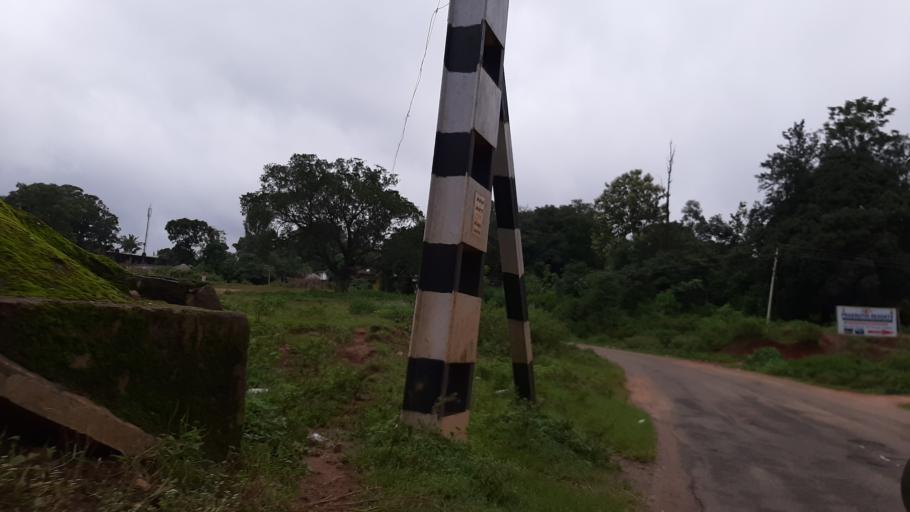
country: IN
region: Andhra Pradesh
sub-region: Vizianagaram District
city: Salur
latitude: 18.3050
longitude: 82.9075
